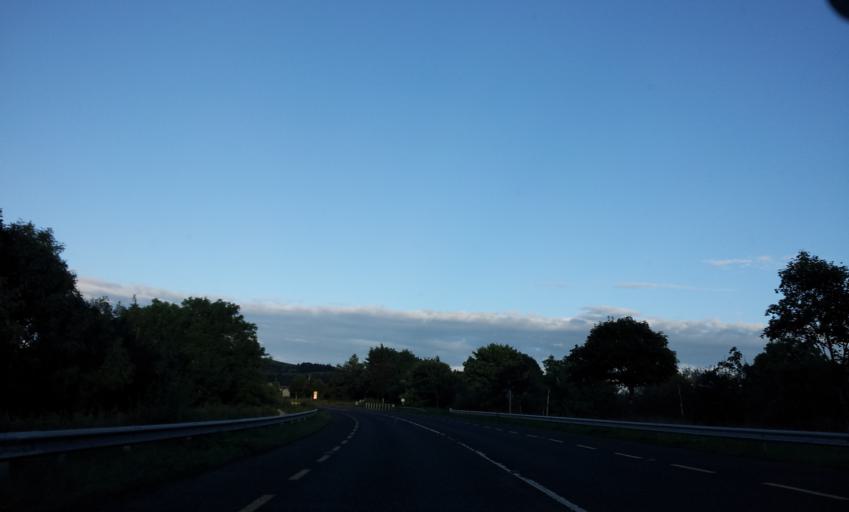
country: IE
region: Munster
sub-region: County Limerick
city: Abbeyfeale
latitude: 52.3826
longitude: -9.2244
